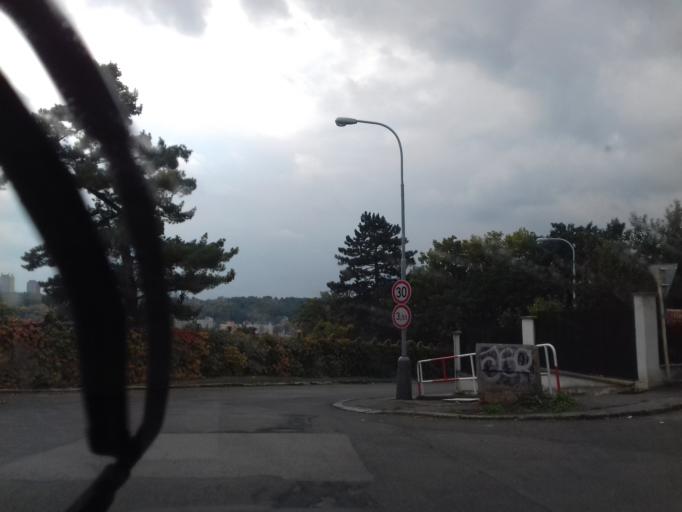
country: CZ
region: Praha
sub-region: Praha 4
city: Hodkovicky
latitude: 50.0379
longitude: 14.4285
